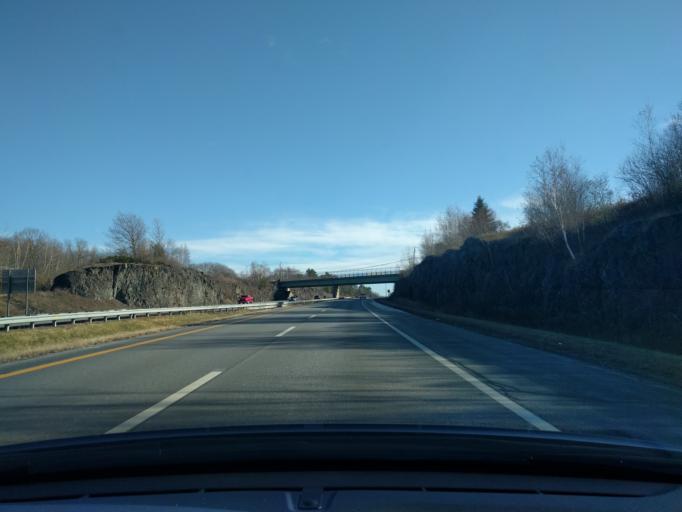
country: US
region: Maine
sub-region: Penobscot County
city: Brewer
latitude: 44.7813
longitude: -68.7614
